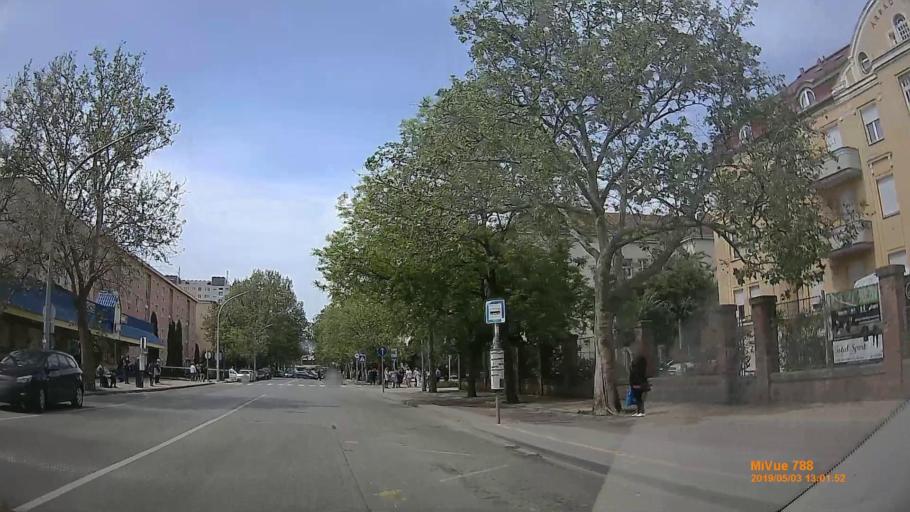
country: HU
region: Jasz-Nagykun-Szolnok
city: Szolnok
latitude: 47.1777
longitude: 20.1815
